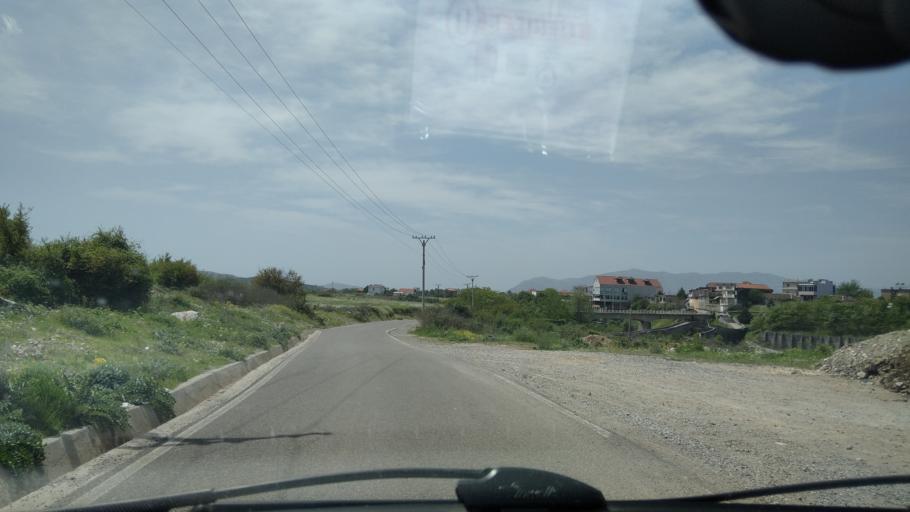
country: AL
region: Shkoder
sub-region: Rrethi i Shkodres
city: Guri i Zi
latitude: 42.1157
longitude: 19.5776
